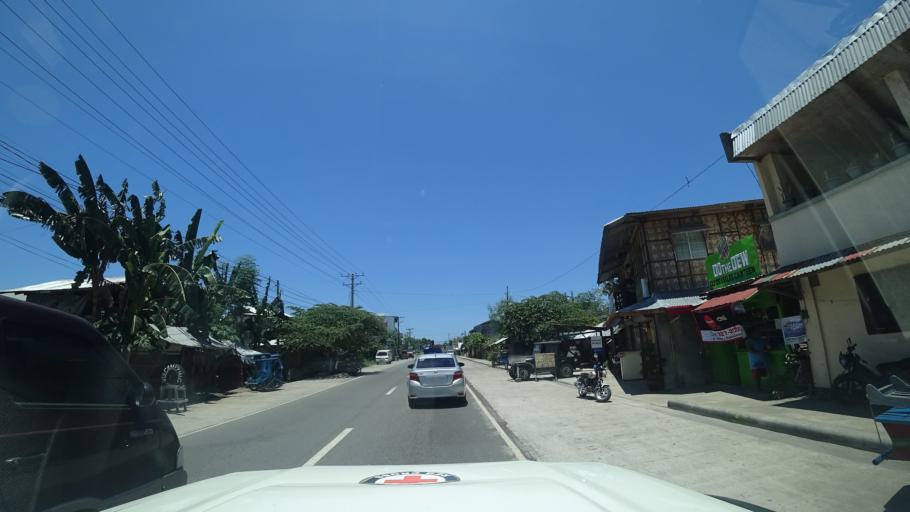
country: PH
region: Eastern Visayas
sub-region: Province of Leyte
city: Pawing
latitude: 11.1807
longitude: 125.0010
